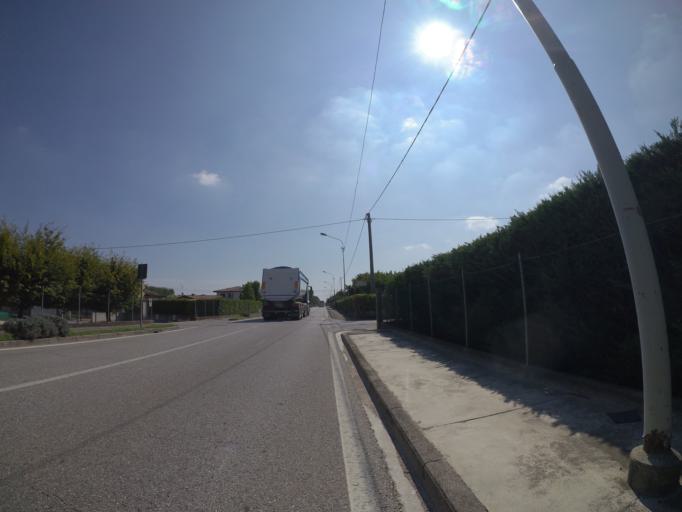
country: IT
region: Friuli Venezia Giulia
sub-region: Provincia di Udine
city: Pocenia
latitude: 45.8288
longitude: 13.1003
